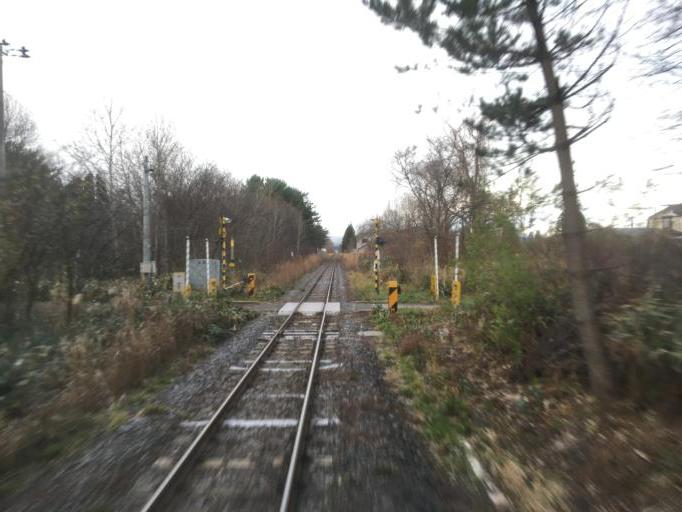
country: JP
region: Aomori
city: Mutsu
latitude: 41.2695
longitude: 141.2072
